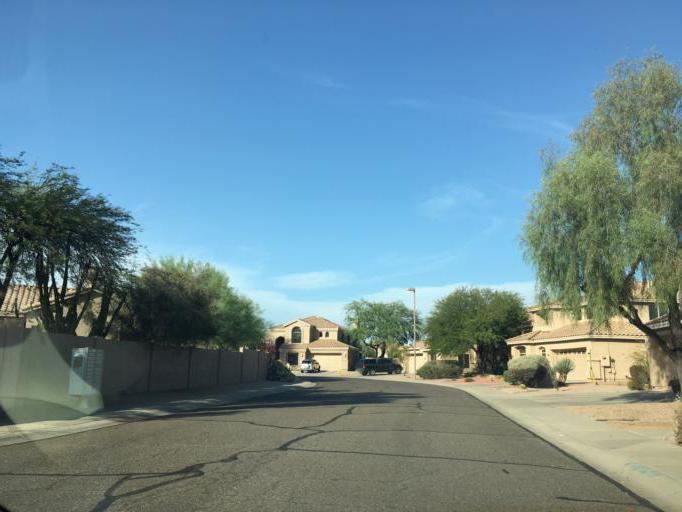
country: US
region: Arizona
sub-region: Maricopa County
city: Carefree
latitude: 33.6859
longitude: -111.9818
